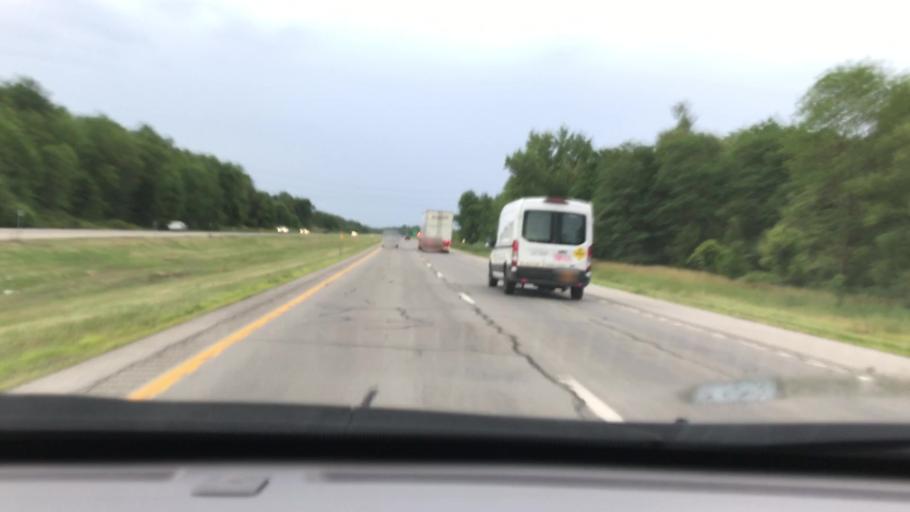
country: US
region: New York
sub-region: Erie County
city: North Boston
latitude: 42.7267
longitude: -78.7737
